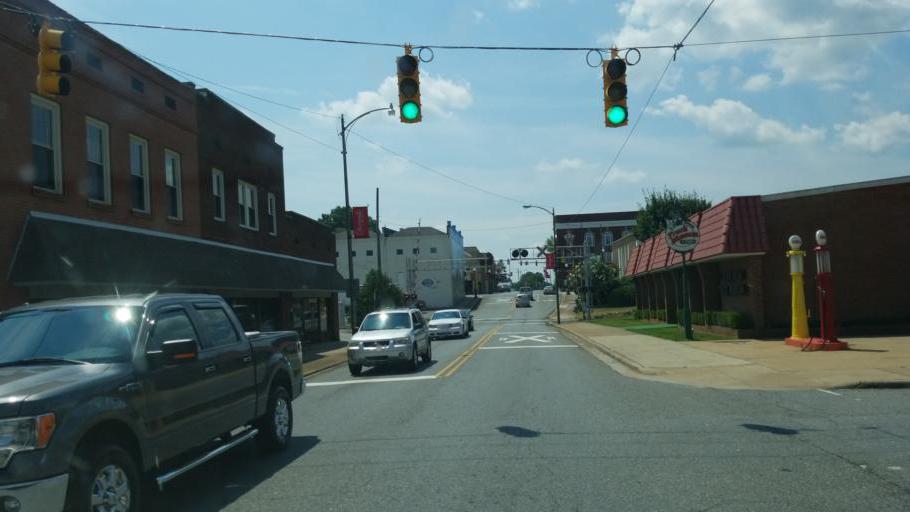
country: US
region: North Carolina
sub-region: Gaston County
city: Cherryville
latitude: 35.3801
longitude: -81.3801
